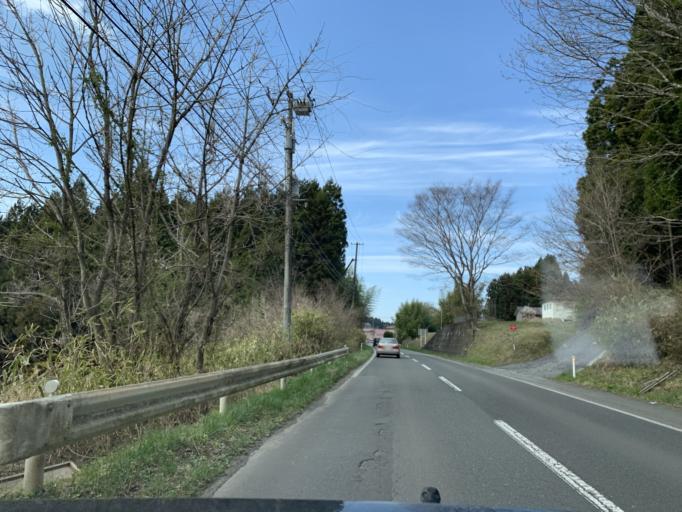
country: JP
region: Iwate
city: Ichinoseki
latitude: 38.8538
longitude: 141.3494
